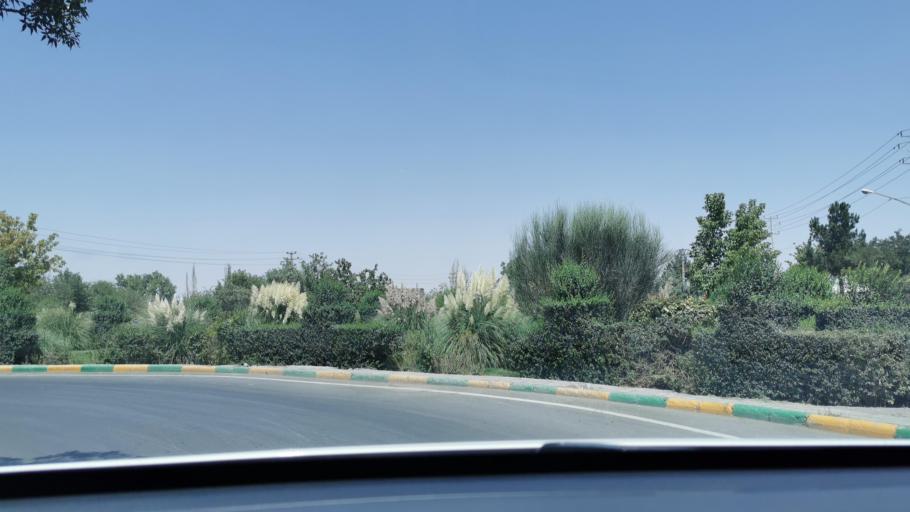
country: IR
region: Razavi Khorasan
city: Mashhad
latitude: 36.3560
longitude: 59.6317
